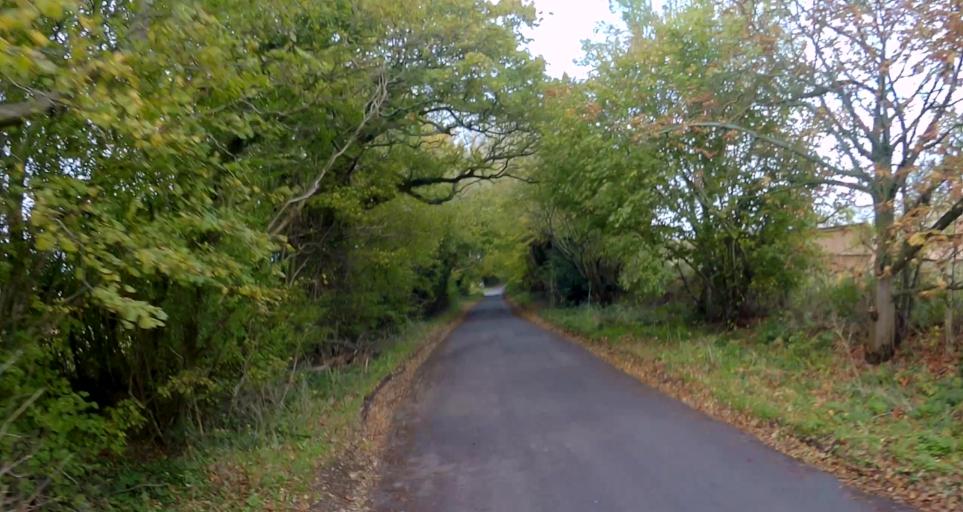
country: GB
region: England
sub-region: Hampshire
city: Four Marks
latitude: 51.1500
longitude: -1.0890
